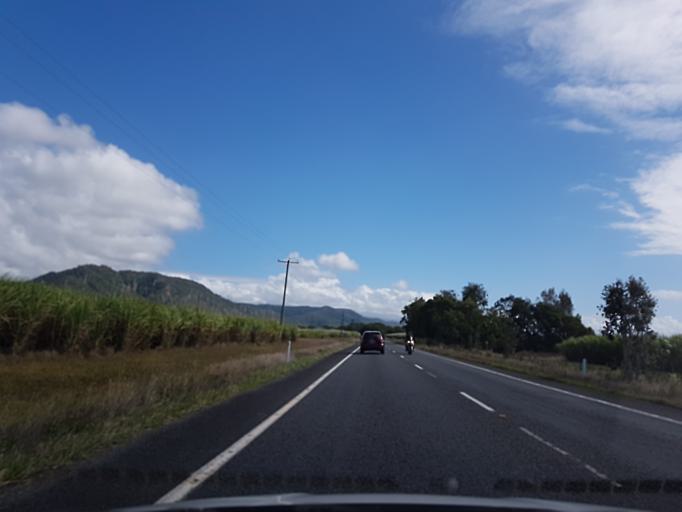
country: AU
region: Queensland
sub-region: Cairns
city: Port Douglas
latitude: -16.5567
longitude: 145.4889
